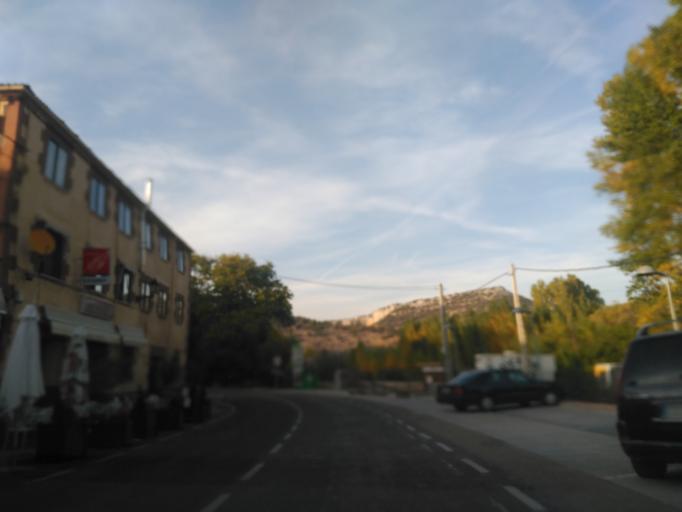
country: ES
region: Castille and Leon
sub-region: Provincia de Soria
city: Ucero
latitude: 41.7179
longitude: -3.0499
